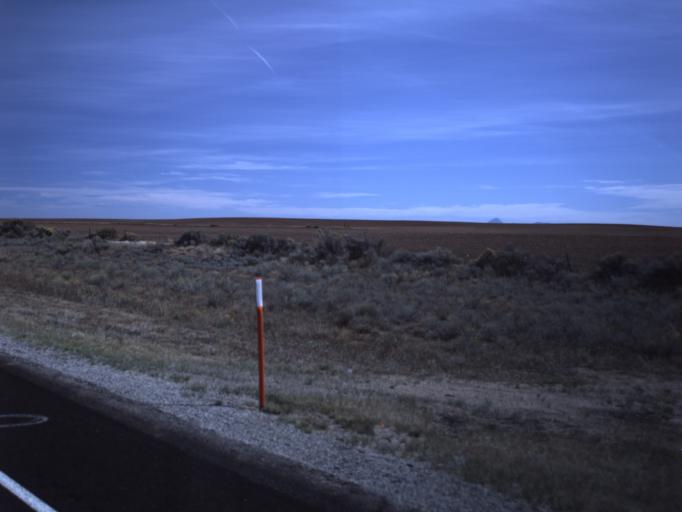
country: US
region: Colorado
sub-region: Dolores County
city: Dove Creek
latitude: 37.8204
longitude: -109.0558
